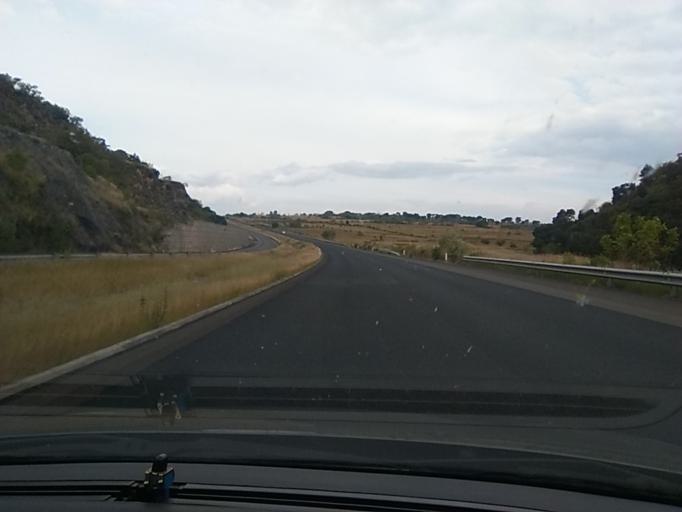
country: MX
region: Mexico
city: Huaniqueo de Morales
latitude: 19.8836
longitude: -101.4455
